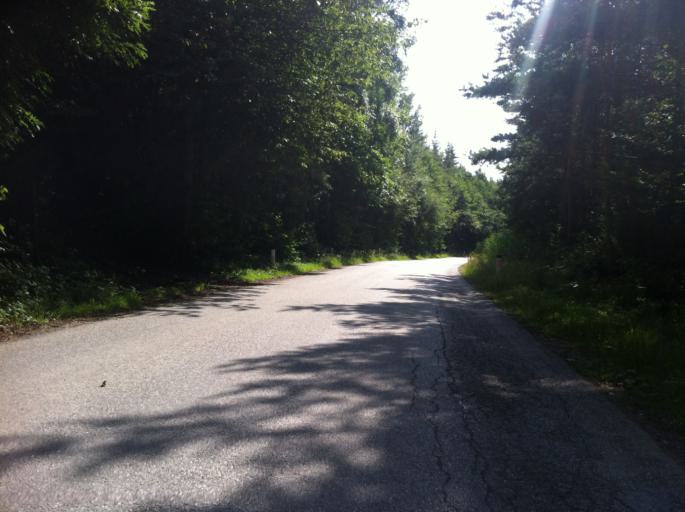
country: AT
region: Lower Austria
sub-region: Politischer Bezirk Wien-Umgebung
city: Wolfsgraben
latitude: 48.1741
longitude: 16.1477
